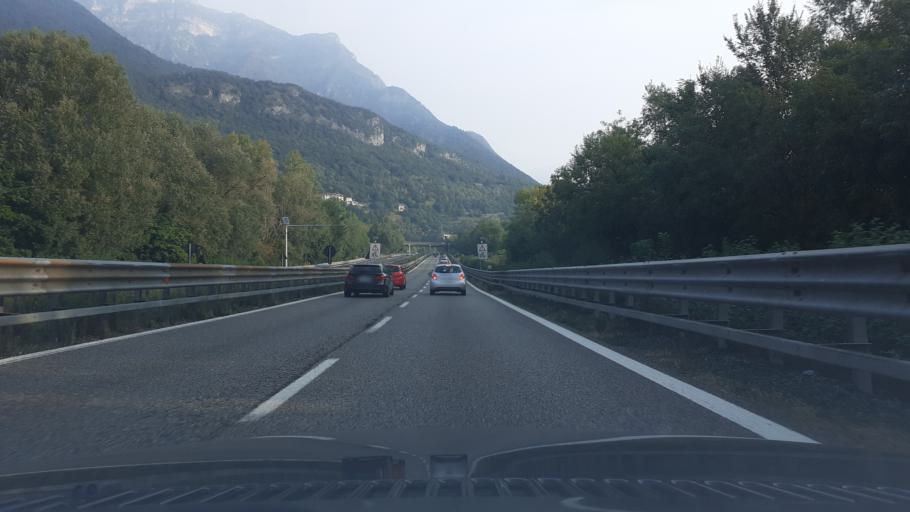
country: IT
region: Lombardy
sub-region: Provincia di Lecco
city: Suello
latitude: 45.8160
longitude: 9.3210
